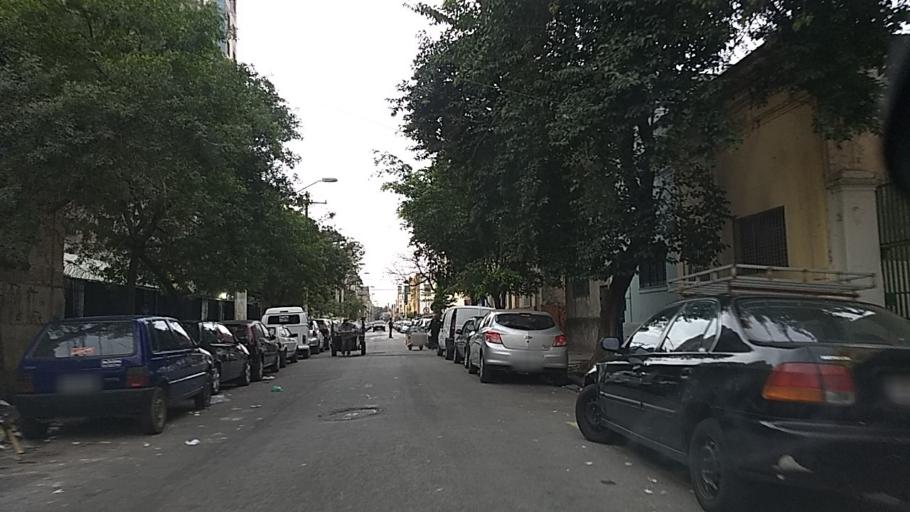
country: BR
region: Sao Paulo
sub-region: Sao Paulo
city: Sao Paulo
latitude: -23.5340
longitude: -46.6242
